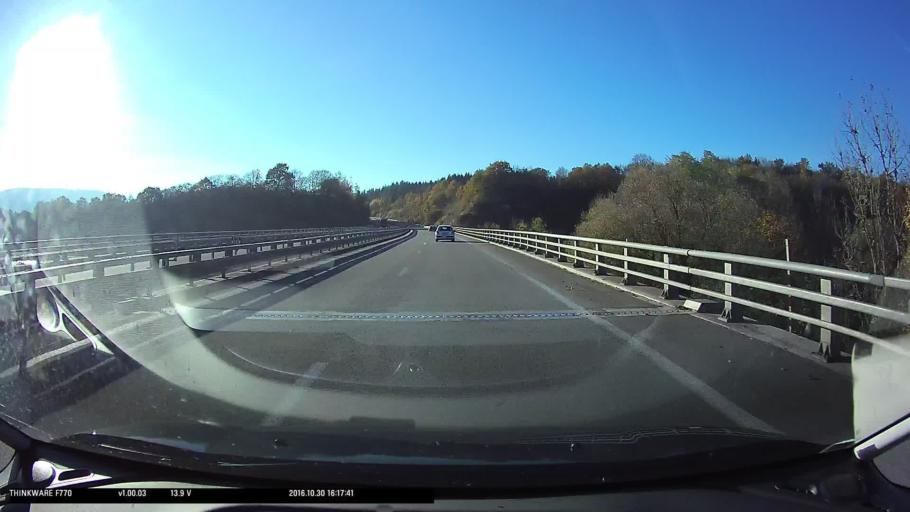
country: FR
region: Franche-Comte
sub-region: Departement du Doubs
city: Clerval
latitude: 47.4121
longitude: 6.5150
